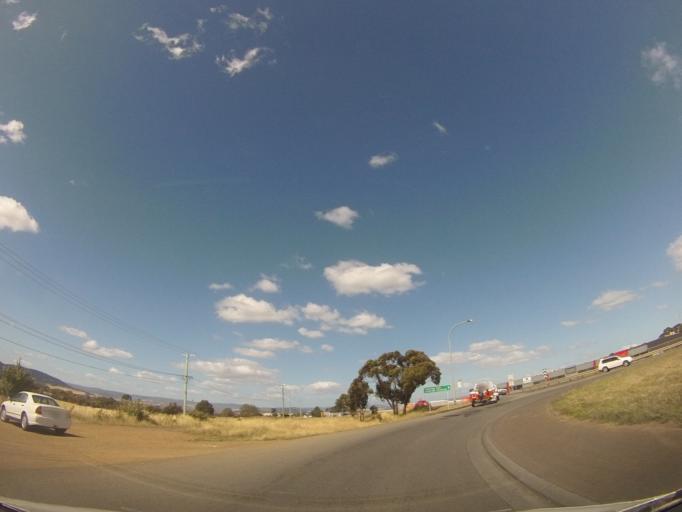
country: AU
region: Tasmania
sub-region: Clarence
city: Cambridge
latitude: -42.8338
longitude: 147.4551
